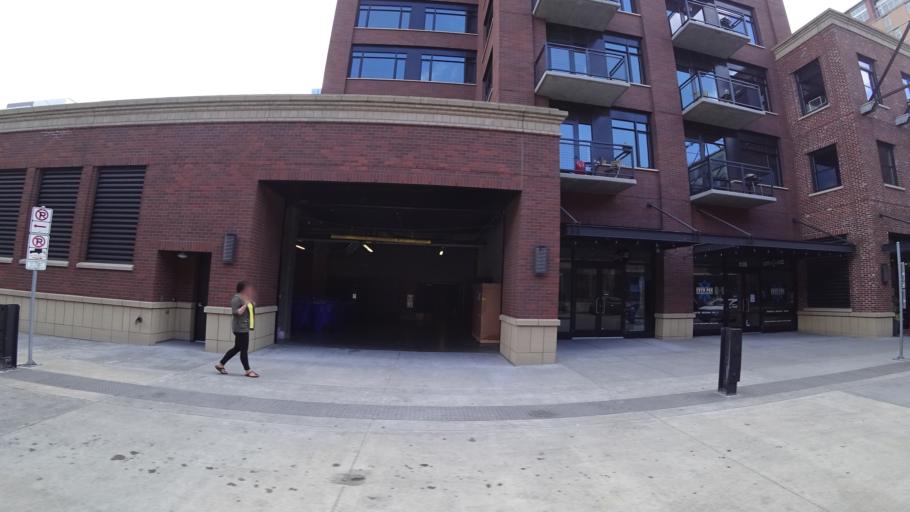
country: US
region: Oregon
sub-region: Multnomah County
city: Portland
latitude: 45.5312
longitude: -122.6844
